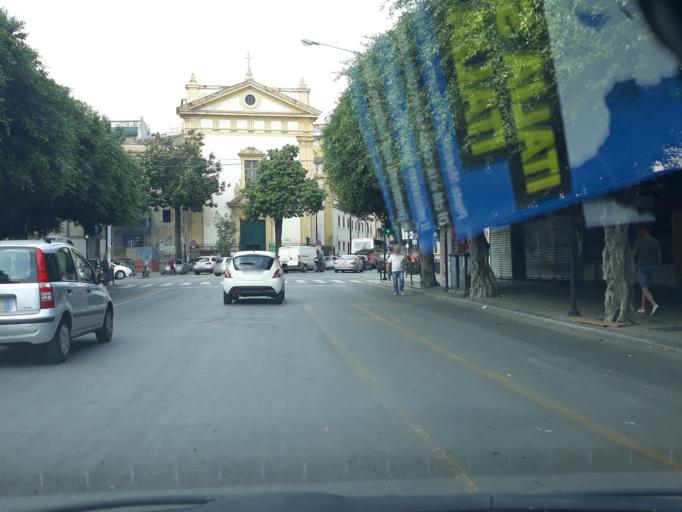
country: IT
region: Sicily
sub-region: Palermo
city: Palermo
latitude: 38.1103
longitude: 13.3656
